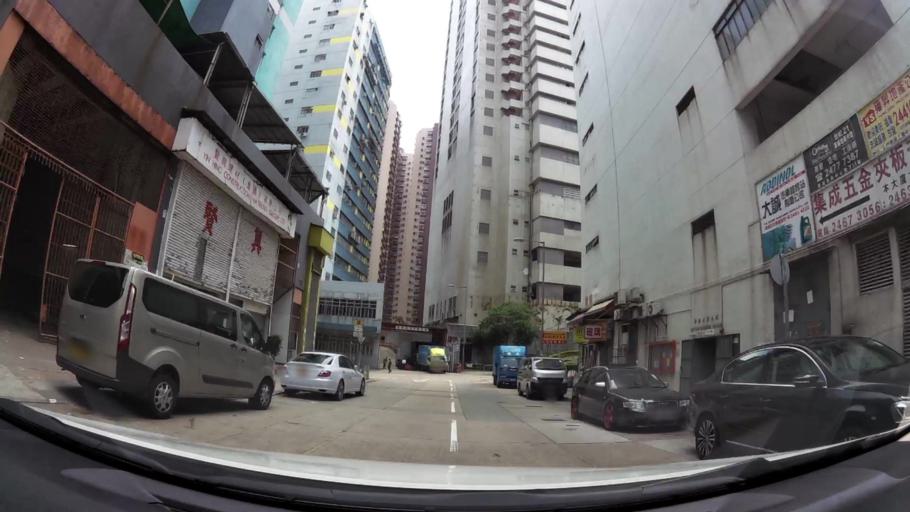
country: HK
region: Tuen Mun
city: Tuen Mun
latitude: 22.4003
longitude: 113.9694
